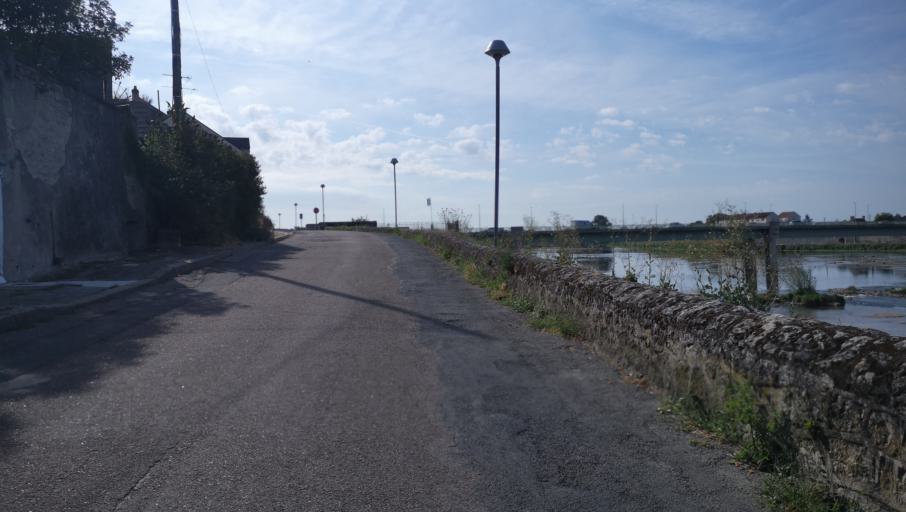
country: FR
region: Centre
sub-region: Departement du Loiret
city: Jargeau
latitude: 47.8709
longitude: 2.1241
